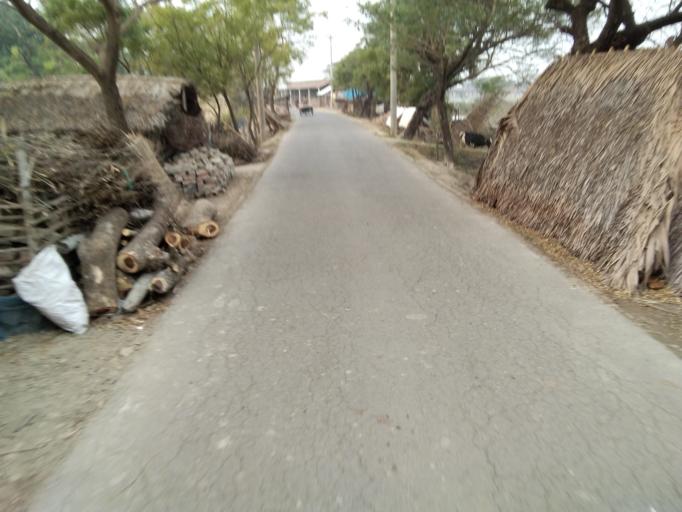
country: BD
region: Khulna
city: Satkhira
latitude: 22.5862
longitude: 89.0657
